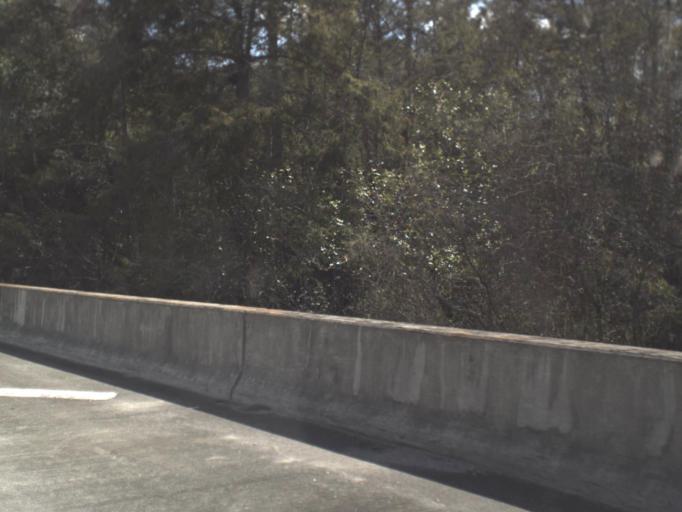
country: US
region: Florida
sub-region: Okeechobee County
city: Okeechobee
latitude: 27.3785
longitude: -80.9875
